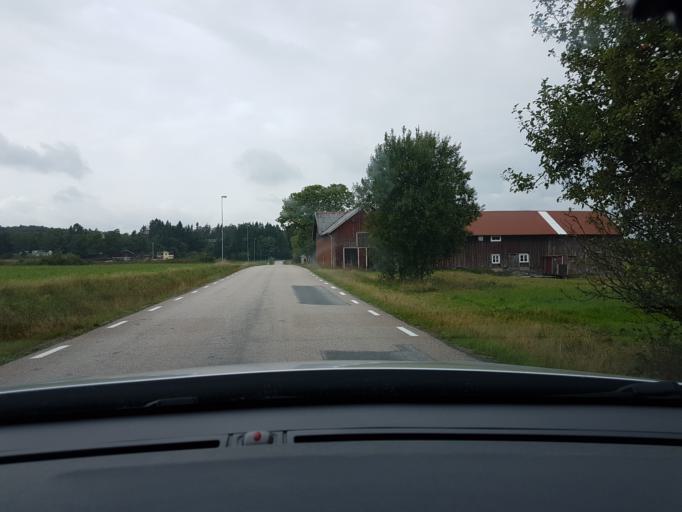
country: SE
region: Vaestra Goetaland
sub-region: Ale Kommun
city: Alvangen
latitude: 57.9170
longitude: 12.1397
